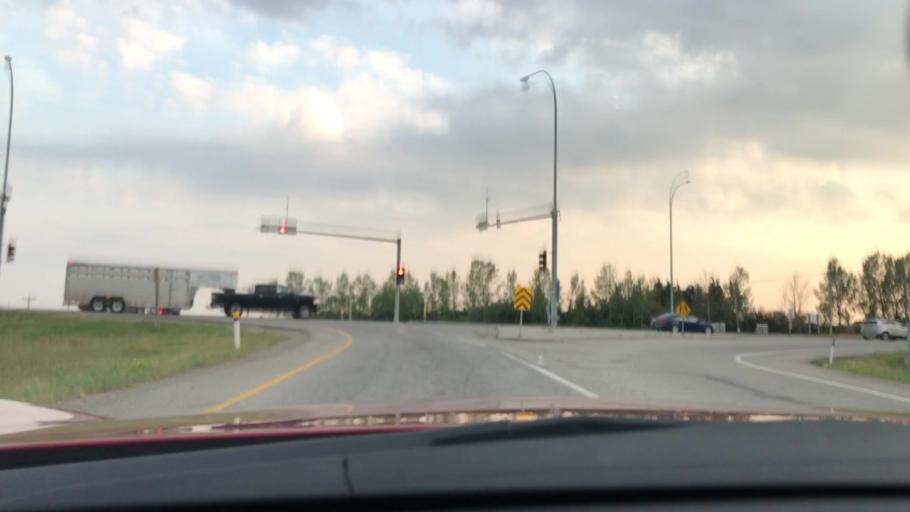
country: CA
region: Alberta
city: Airdrie
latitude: 51.2130
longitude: -114.0037
